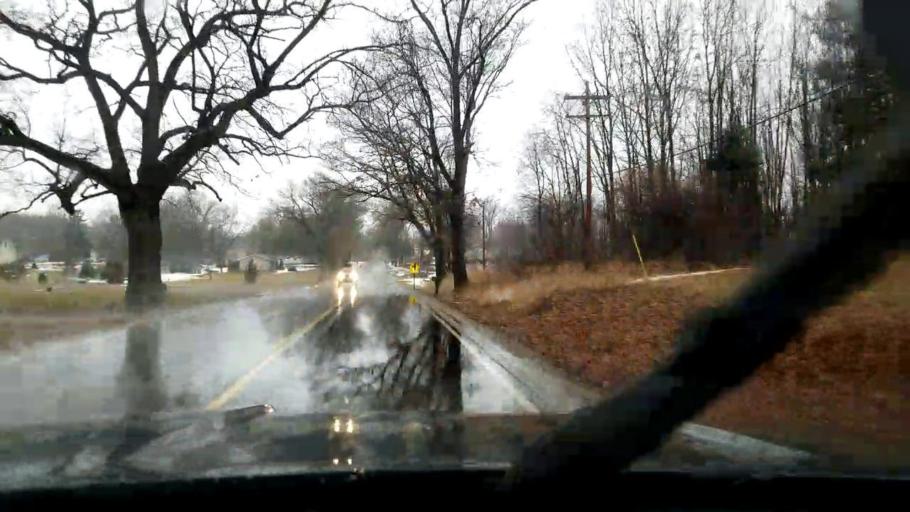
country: US
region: Michigan
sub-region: Jackson County
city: Michigan Center
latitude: 42.2842
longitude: -84.3493
